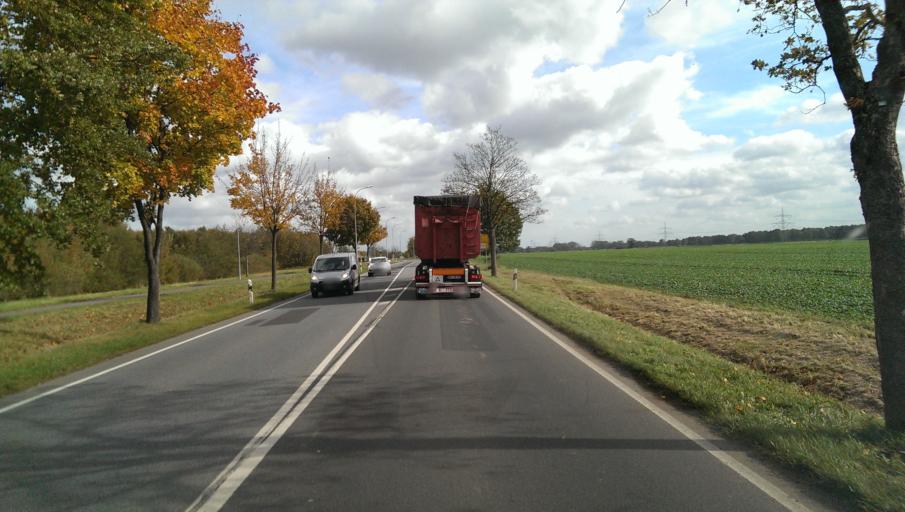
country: DE
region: Brandenburg
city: Schwarzheide
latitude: 51.4707
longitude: 13.8212
